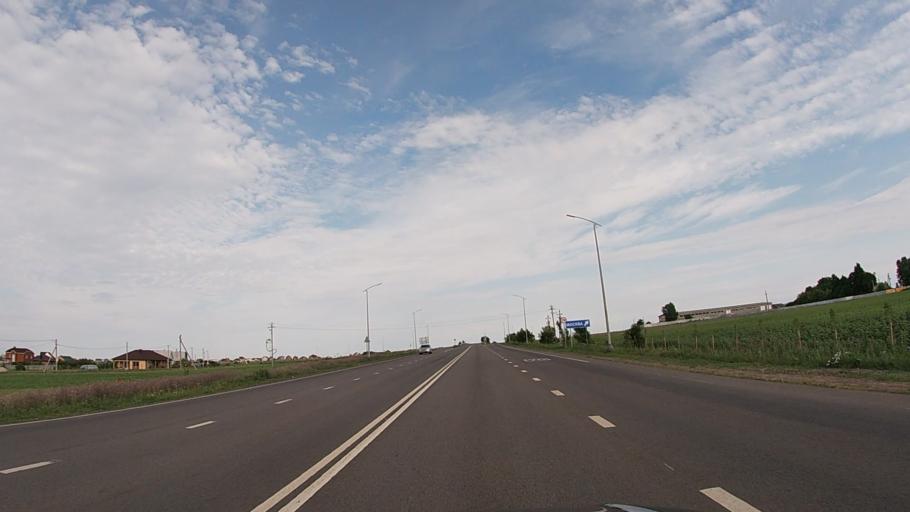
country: RU
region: Belgorod
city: Severnyy
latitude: 50.6724
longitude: 36.4794
